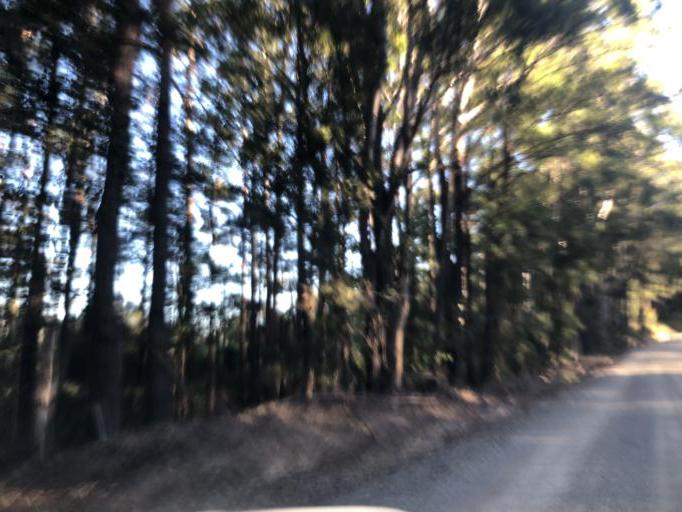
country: AU
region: New South Wales
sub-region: Nambucca Shire
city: Nambucca
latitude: -30.5850
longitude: 152.9321
